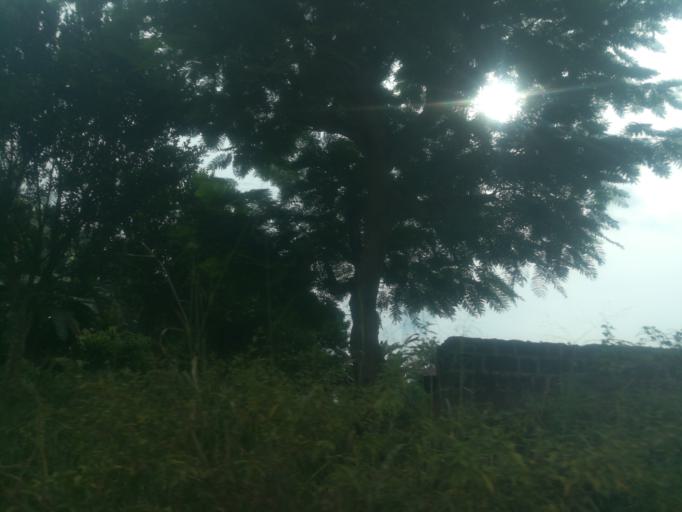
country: NG
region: Ogun
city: Ayetoro
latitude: 7.2837
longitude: 3.0885
